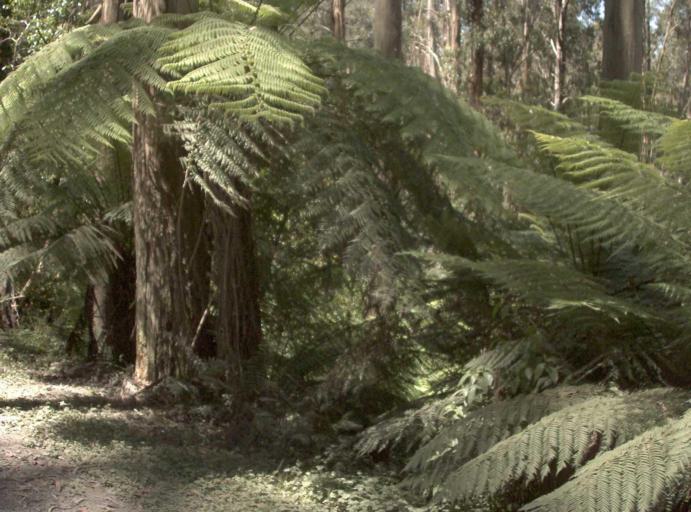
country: AU
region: Victoria
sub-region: Yarra Ranges
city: Millgrove
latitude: -37.6800
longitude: 145.7225
